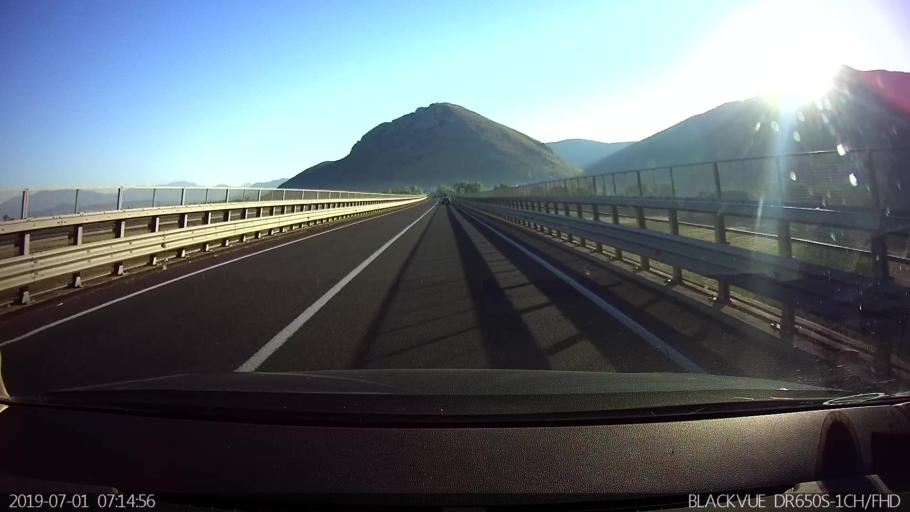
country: IT
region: Latium
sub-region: Provincia di Latina
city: Borgo Hermada
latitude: 41.3267
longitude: 13.1886
